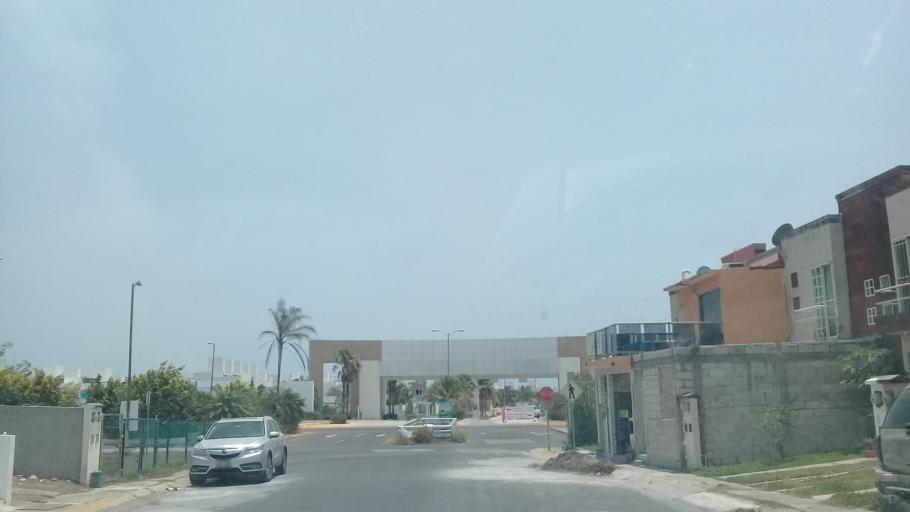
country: MX
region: Veracruz
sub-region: Veracruz
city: Hacienda Sotavento
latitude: 19.1332
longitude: -96.1747
